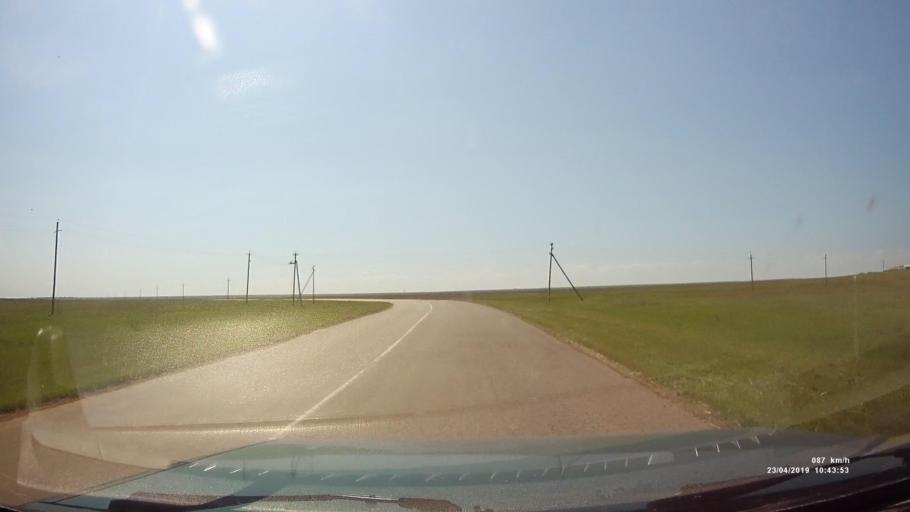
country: RU
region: Kalmykiya
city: Yashalta
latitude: 46.4647
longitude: 42.6502
